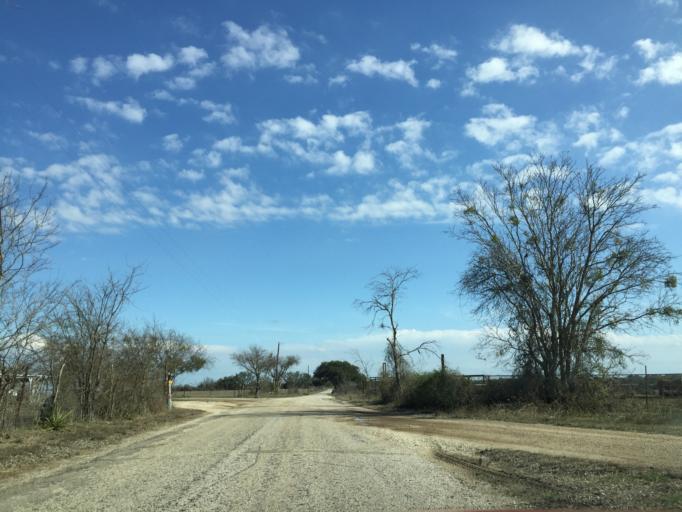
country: US
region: Texas
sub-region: Williamson County
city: Florence
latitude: 30.7824
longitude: -97.8951
